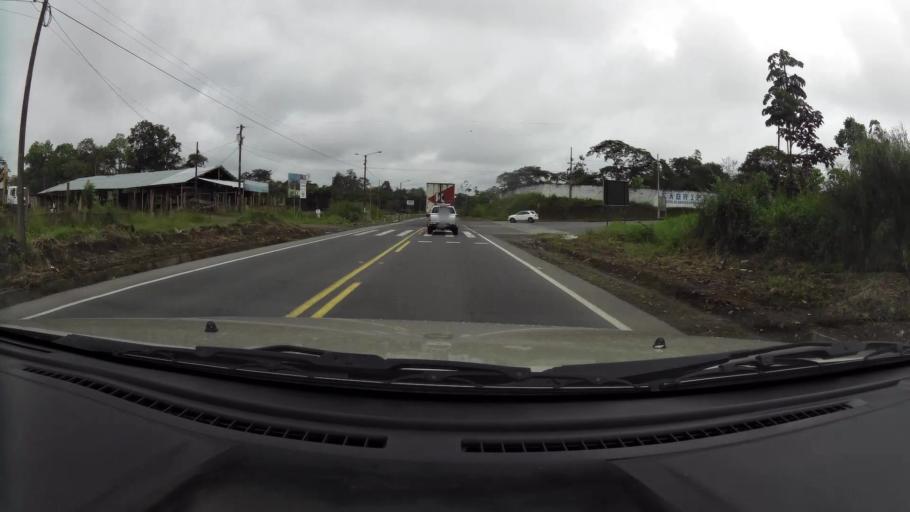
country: EC
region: Santo Domingo de los Tsachilas
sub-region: Canton Santo Domingo de los Colorados
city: Santo Domingo de los Colorados
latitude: -0.2630
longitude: -79.1355
